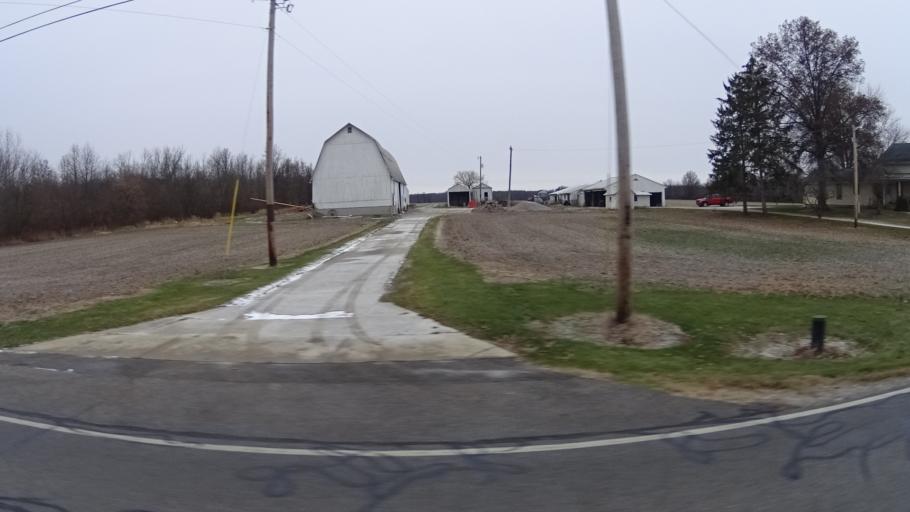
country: US
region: Ohio
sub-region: Lorain County
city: Grafton
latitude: 41.2974
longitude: -82.0359
